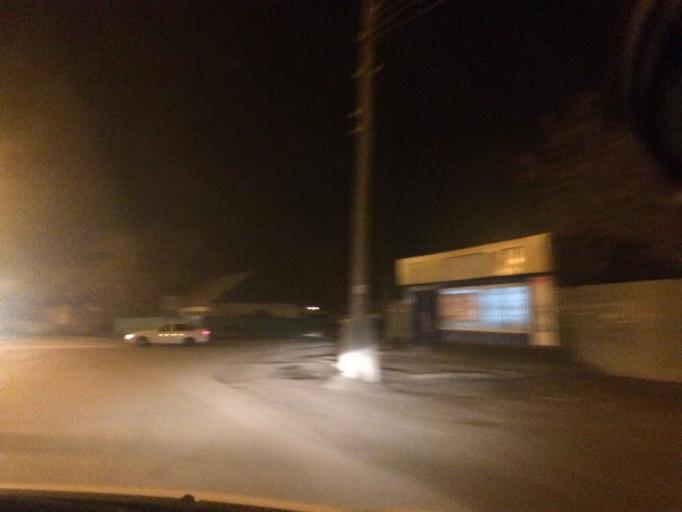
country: KZ
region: Astana Qalasy
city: Astana
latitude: 51.2103
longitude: 71.3933
